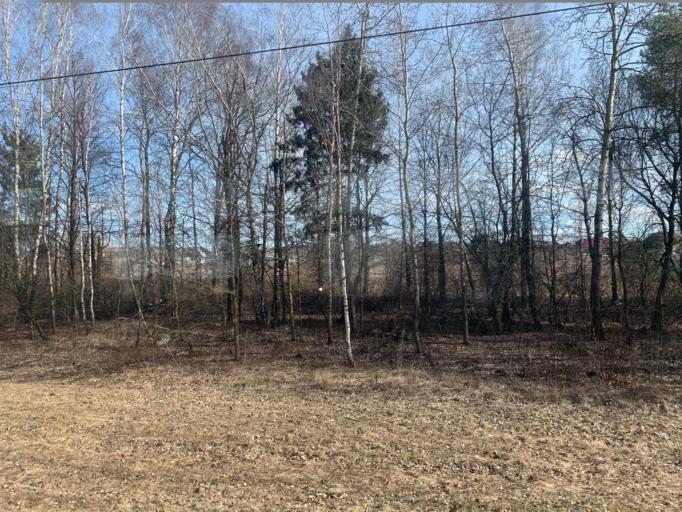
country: BY
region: Minsk
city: Dzyarzhynsk
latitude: 53.6422
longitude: 27.0961
